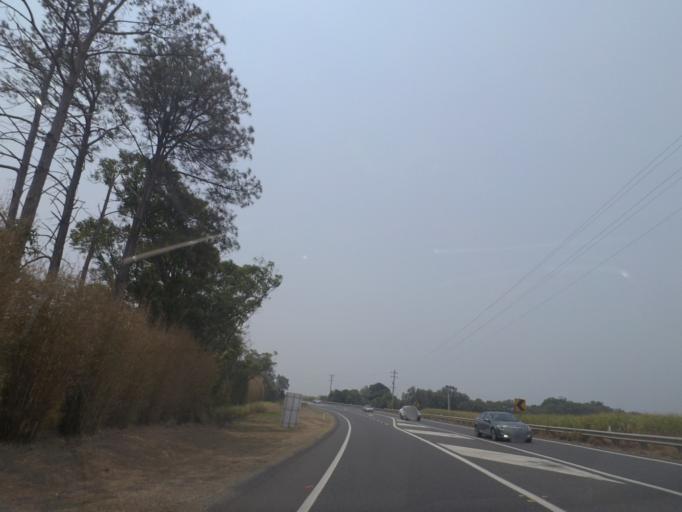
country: AU
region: New South Wales
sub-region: Richmond Valley
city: Evans Head
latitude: -28.9933
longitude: 153.4608
